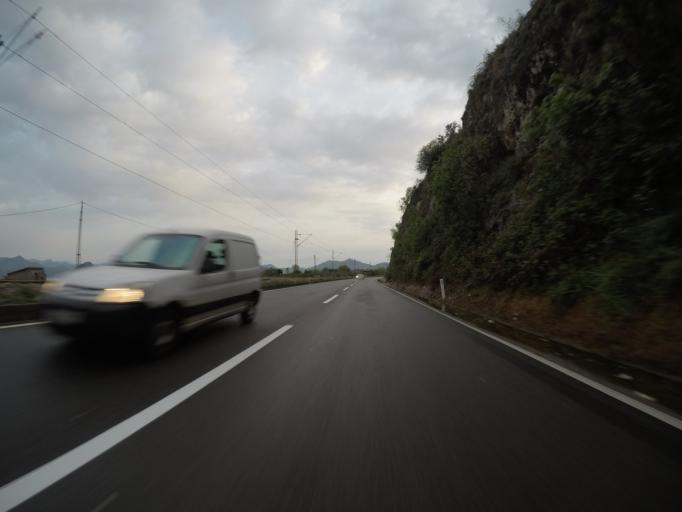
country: ME
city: Mojanovici
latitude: 42.2750
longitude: 19.1247
